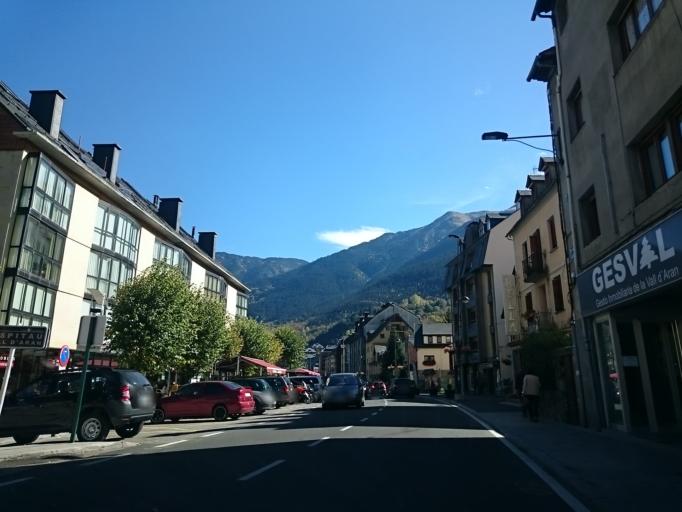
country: ES
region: Catalonia
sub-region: Provincia de Lleida
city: Vielha
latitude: 42.7012
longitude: 0.7966
